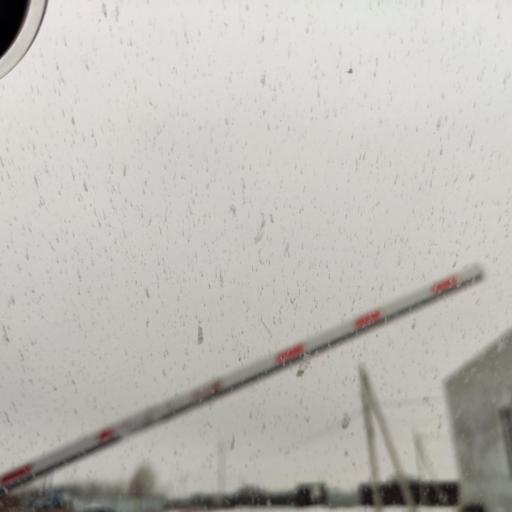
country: RU
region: Voronezj
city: Podgornoye
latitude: 51.8536
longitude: 39.1855
